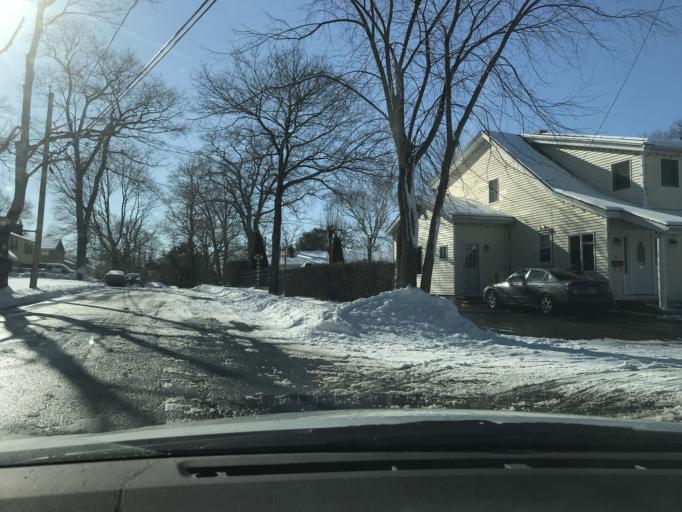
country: US
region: Massachusetts
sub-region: Essex County
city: Saugus
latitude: 42.4745
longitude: -71.0017
